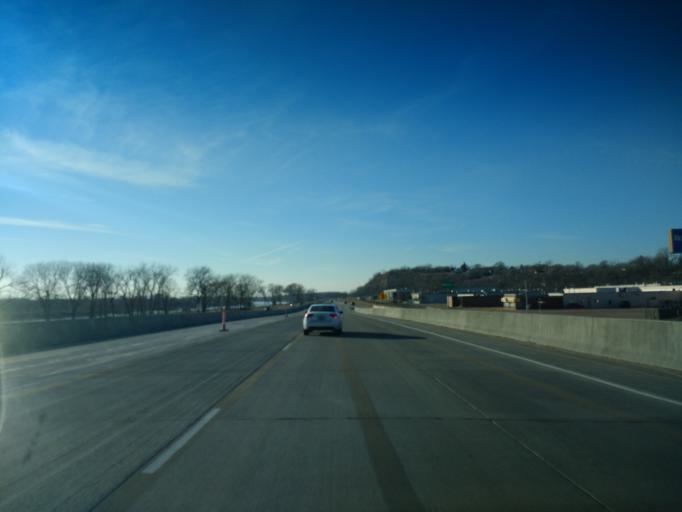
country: US
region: Nebraska
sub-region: Dakota County
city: South Sioux City
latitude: 42.4921
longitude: -96.4253
